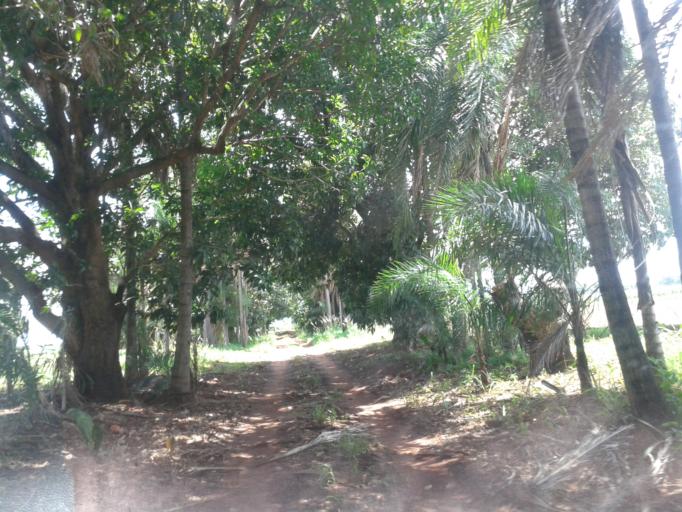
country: BR
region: Minas Gerais
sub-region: Santa Vitoria
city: Santa Vitoria
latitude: -19.1504
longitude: -50.6084
